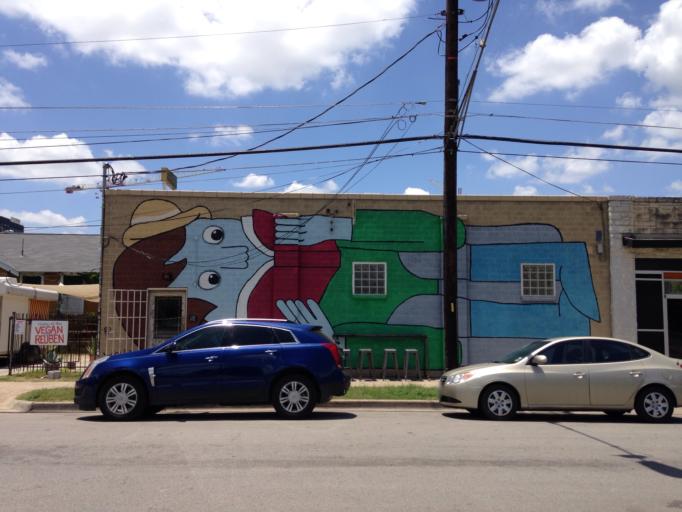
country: US
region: Texas
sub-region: Travis County
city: Austin
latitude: 30.2604
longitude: -97.7346
